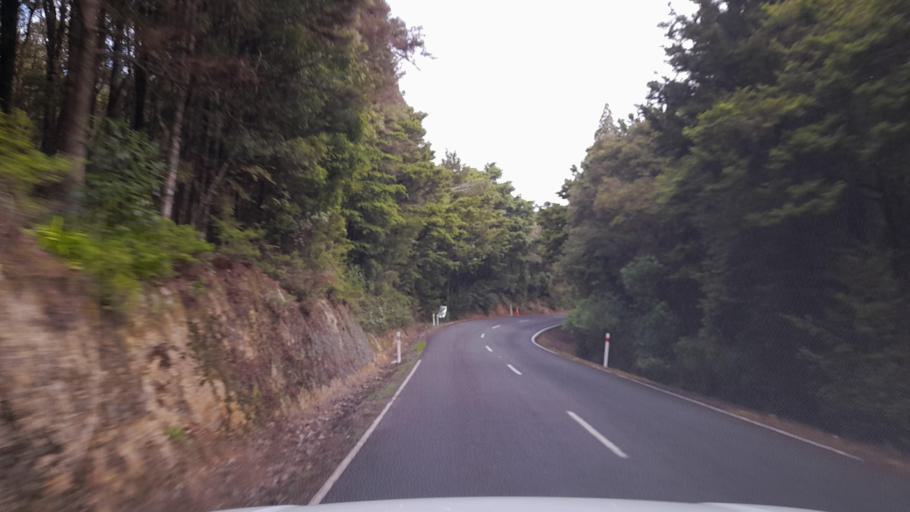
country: NZ
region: Northland
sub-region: Whangarei
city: Maungatapere
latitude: -35.7652
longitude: 174.2424
